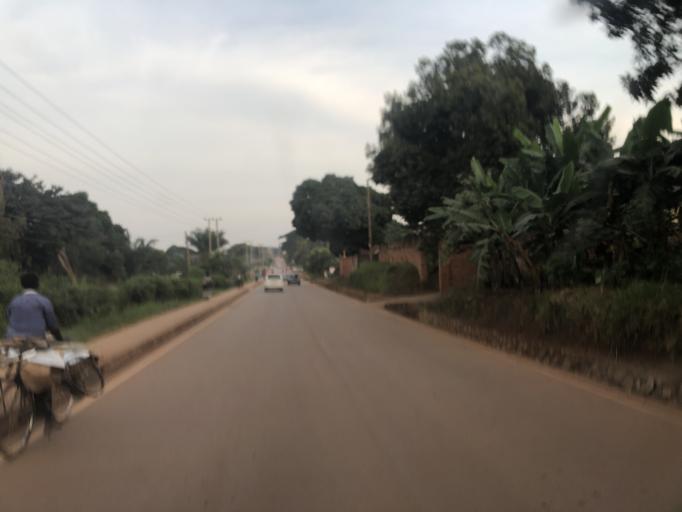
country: UG
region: Central Region
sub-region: Kampala District
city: Kampala
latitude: 0.2797
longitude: 32.5410
